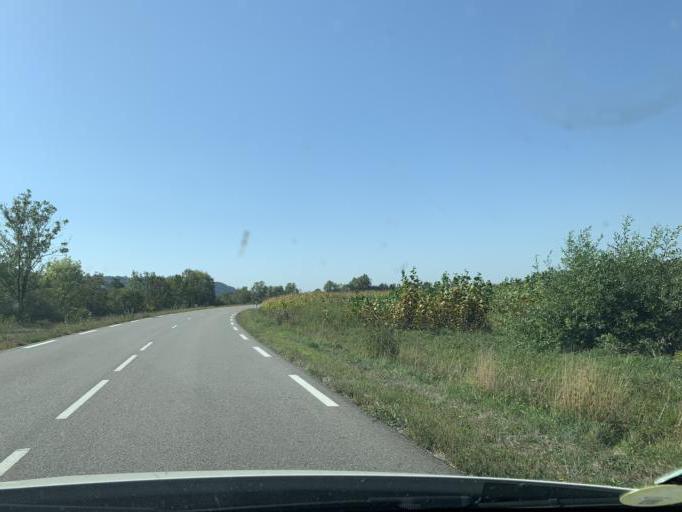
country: FR
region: Rhone-Alpes
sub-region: Departement de la Savoie
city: Saint-Genix-sur-Guiers
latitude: 45.6437
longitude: 5.6854
